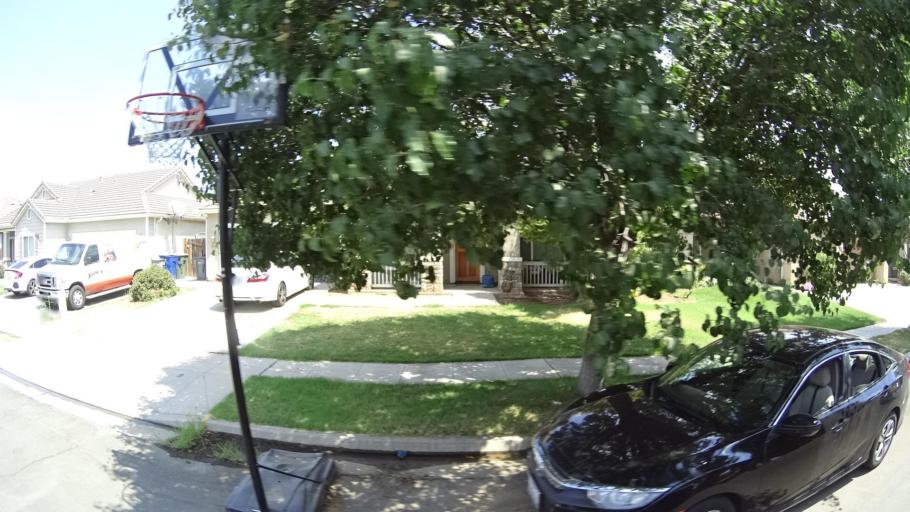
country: US
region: California
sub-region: Fresno County
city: Tarpey Village
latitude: 36.7826
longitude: -119.6796
